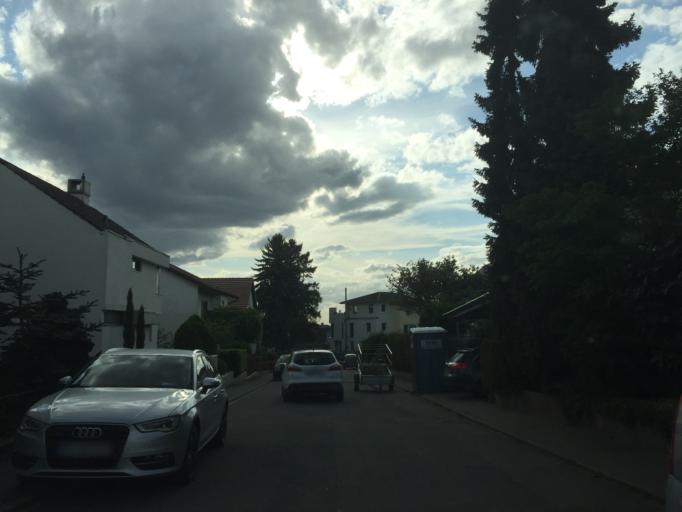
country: DE
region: Baden-Wuerttemberg
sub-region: Karlsruhe Region
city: Weinheim
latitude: 49.5226
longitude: 8.6643
